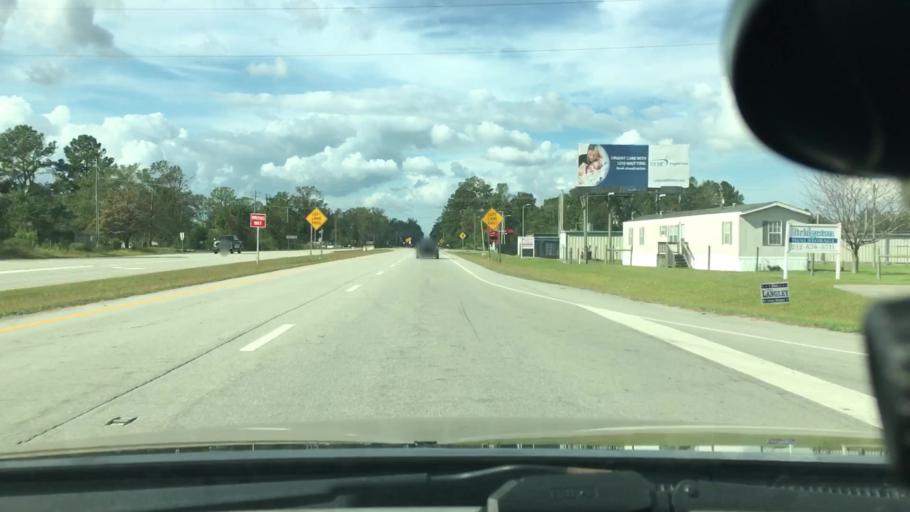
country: US
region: North Carolina
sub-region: Craven County
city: New Bern
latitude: 35.1534
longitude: -77.0351
